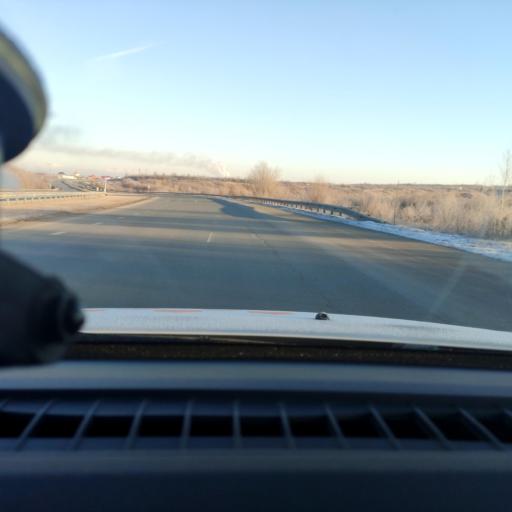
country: RU
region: Samara
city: Novokuybyshevsk
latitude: 53.0568
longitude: 50.0185
